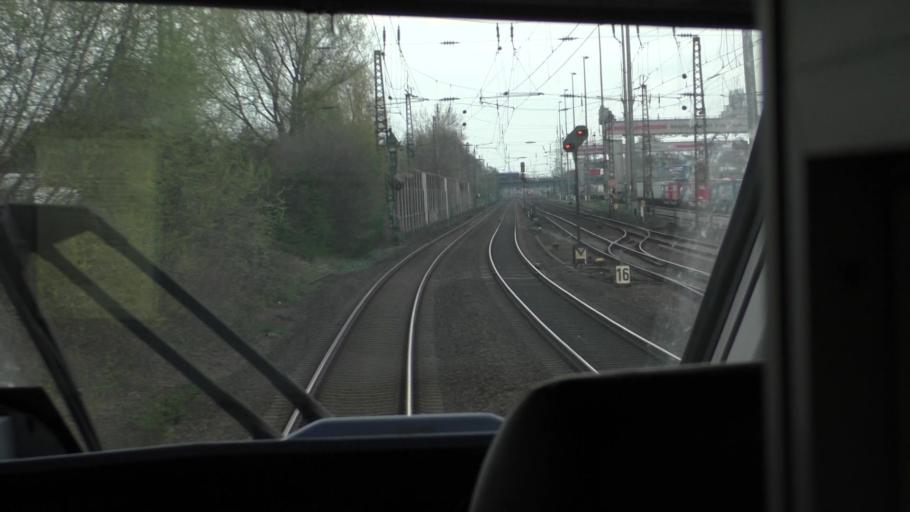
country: DE
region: North Rhine-Westphalia
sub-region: Regierungsbezirk Koln
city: Hurth
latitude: 50.8844
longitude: 6.9141
